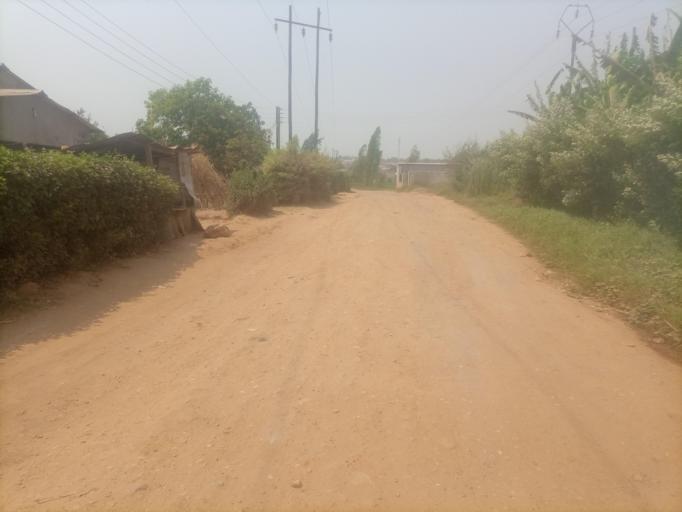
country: ZM
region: Lusaka
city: Lusaka
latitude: -15.3932
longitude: 28.3674
